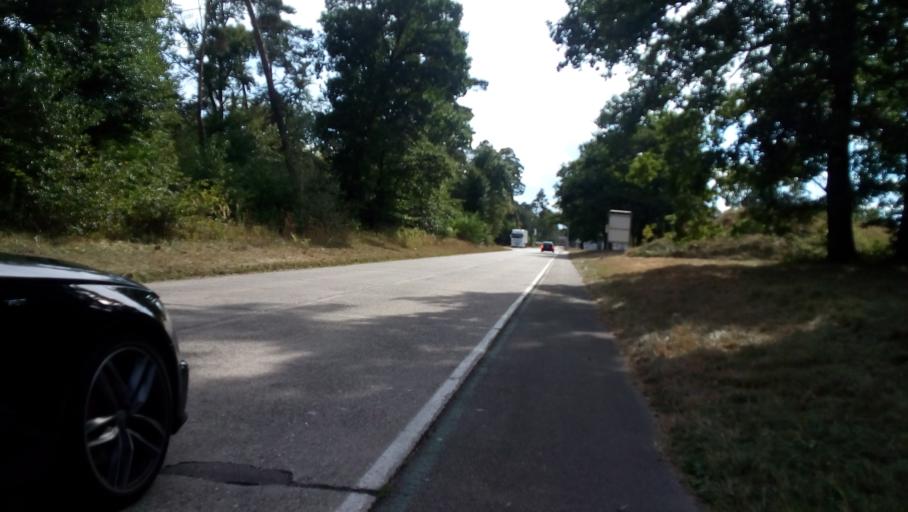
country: DE
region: Baden-Wuerttemberg
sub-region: Karlsruhe Region
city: Hugelsheim
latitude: 48.7740
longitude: 8.0902
